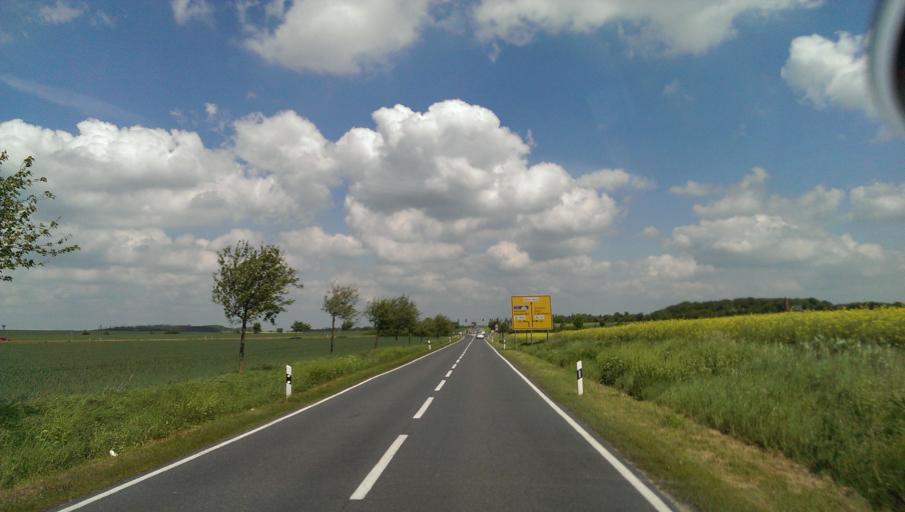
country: DE
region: Saxony-Anhalt
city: Eggersdorf
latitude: 51.9880
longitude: 11.6839
